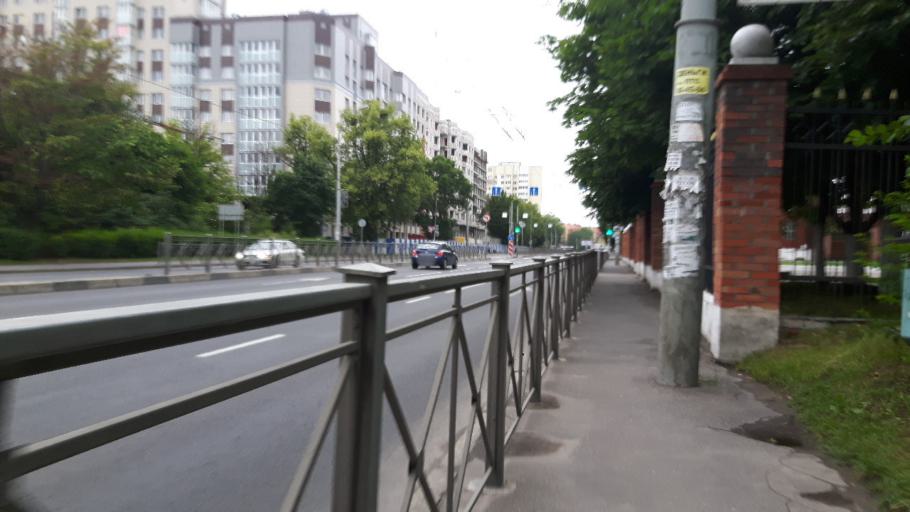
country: RU
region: Kaliningrad
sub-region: Gorod Kaliningrad
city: Kaliningrad
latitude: 54.7331
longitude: 20.4860
